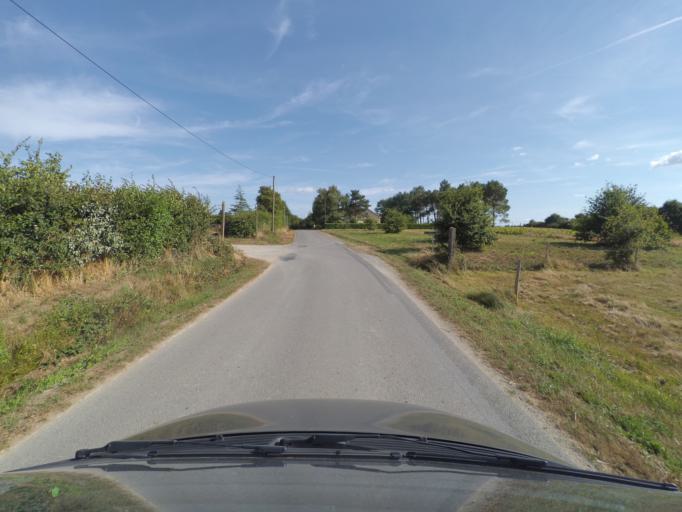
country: FR
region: Pays de la Loire
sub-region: Departement de la Loire-Atlantique
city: Le Bignon
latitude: 47.0944
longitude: -1.4835
